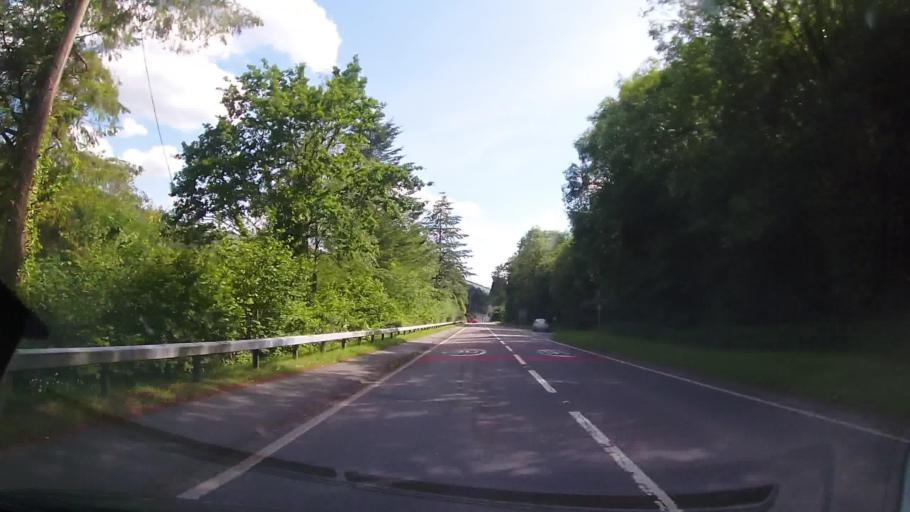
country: GB
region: Wales
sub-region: Gwynedd
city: Corris
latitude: 52.7150
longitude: -3.6910
